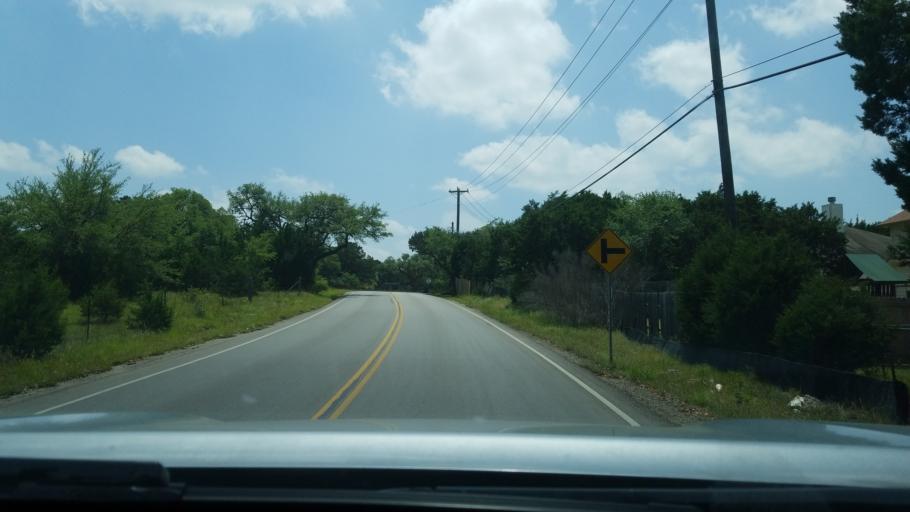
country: US
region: Texas
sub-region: Hays County
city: Woodcreek
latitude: 30.0275
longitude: -98.1291
